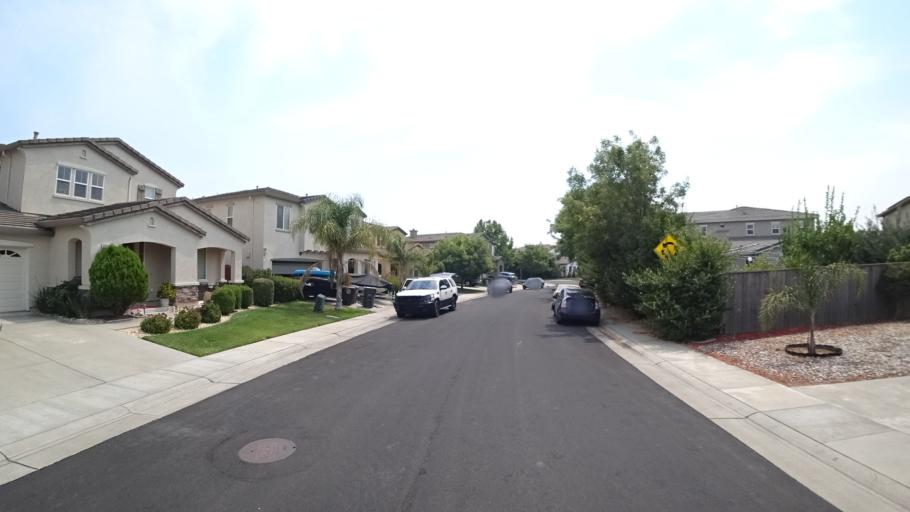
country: US
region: California
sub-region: Sacramento County
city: Laguna
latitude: 38.3861
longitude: -121.4243
